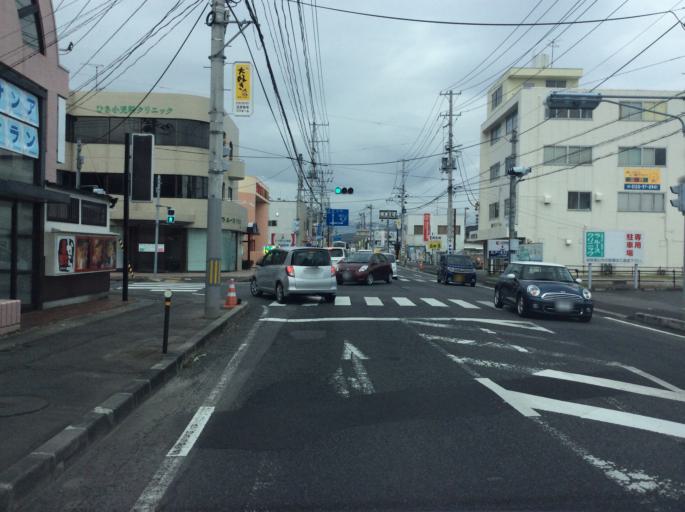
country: JP
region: Fukushima
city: Iwaki
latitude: 37.0499
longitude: 140.9009
